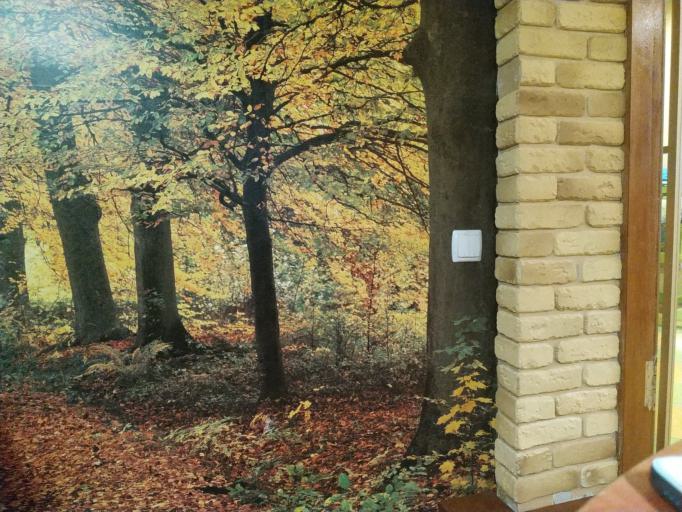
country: RU
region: Novgorod
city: Kulotino
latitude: 58.5327
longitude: 33.2843
